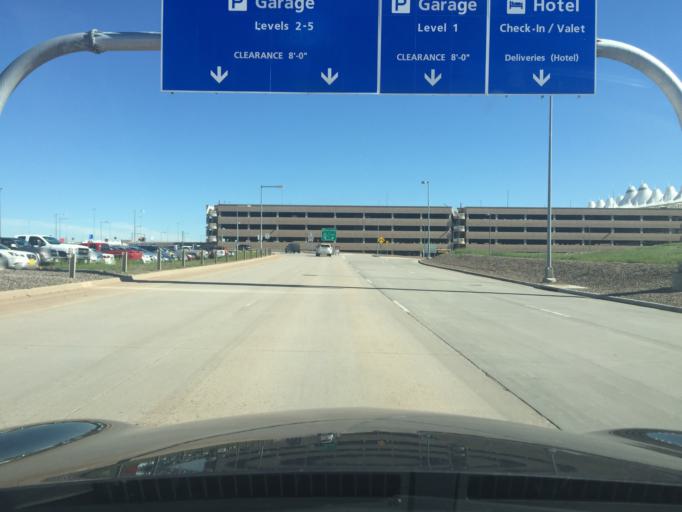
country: US
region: Colorado
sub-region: Weld County
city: Lochbuie
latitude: 39.8455
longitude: -104.6770
